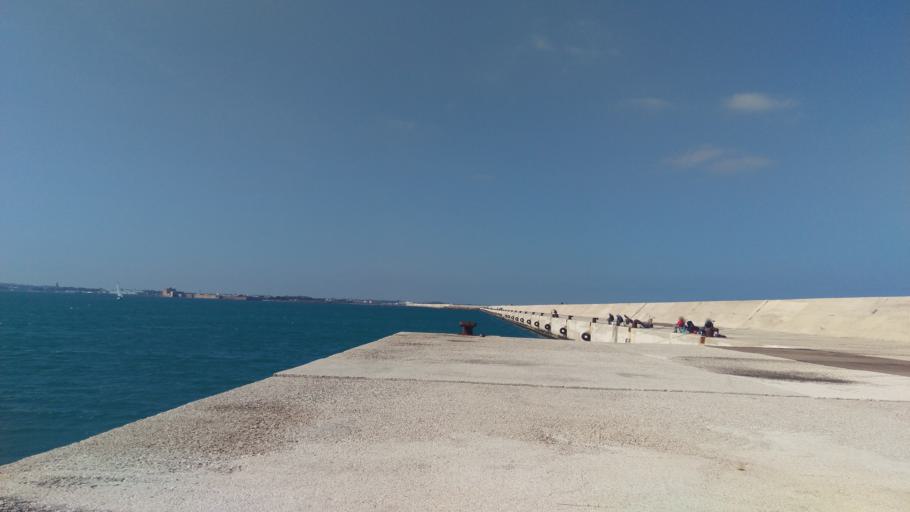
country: IT
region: Apulia
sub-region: Provincia di Brindisi
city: Materdomini
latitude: 40.6629
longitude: 17.9964
